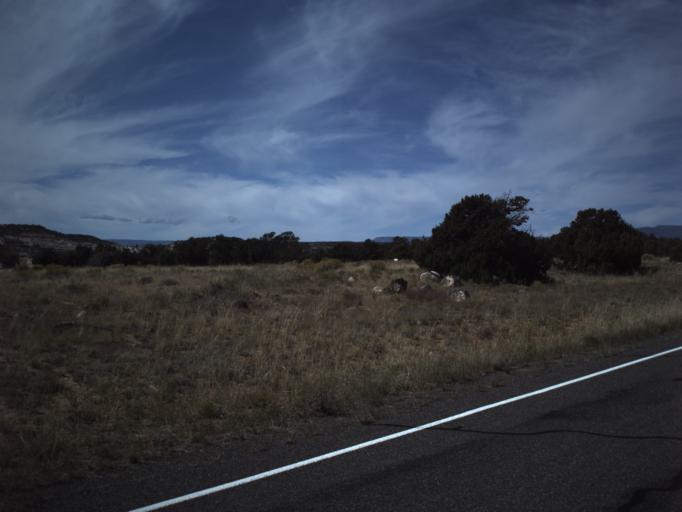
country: US
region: Utah
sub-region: Wayne County
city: Loa
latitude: 37.8445
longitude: -111.4255
